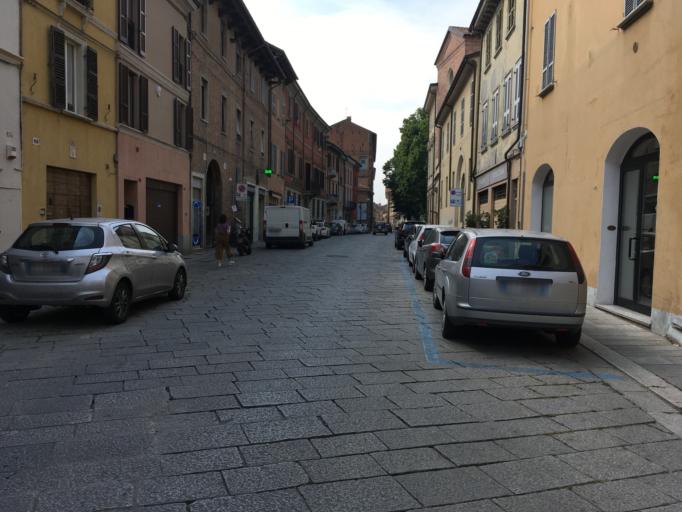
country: IT
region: Emilia-Romagna
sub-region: Provincia di Piacenza
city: Piacenza
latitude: 45.0497
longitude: 9.7019
